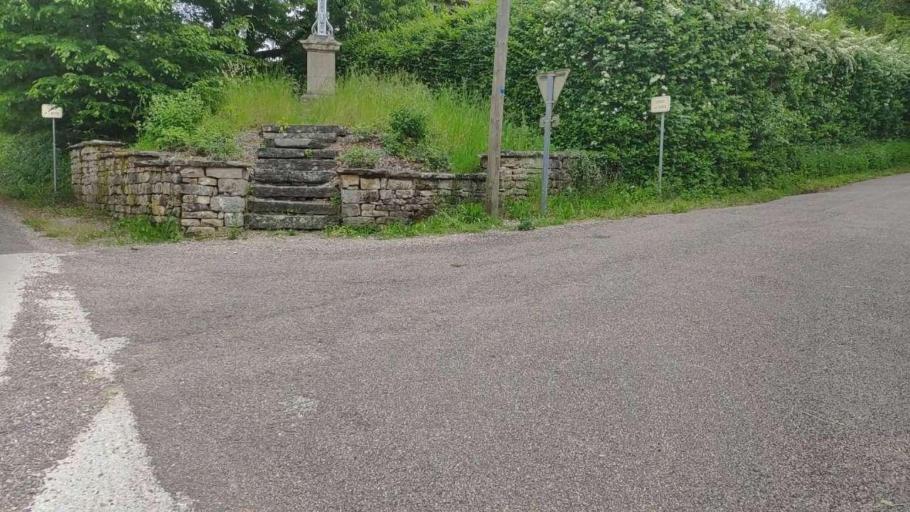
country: FR
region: Franche-Comte
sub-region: Departement du Jura
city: Montmorot
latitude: 46.7587
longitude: 5.5611
